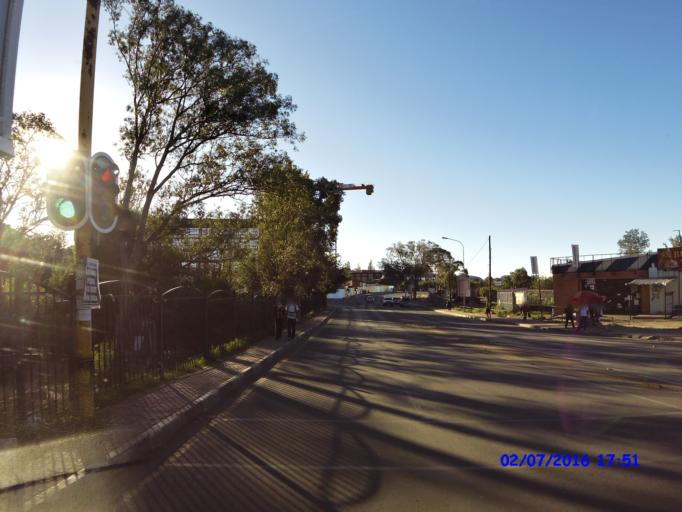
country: LS
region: Maseru
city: Maseru
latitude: -29.3132
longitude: 27.4913
